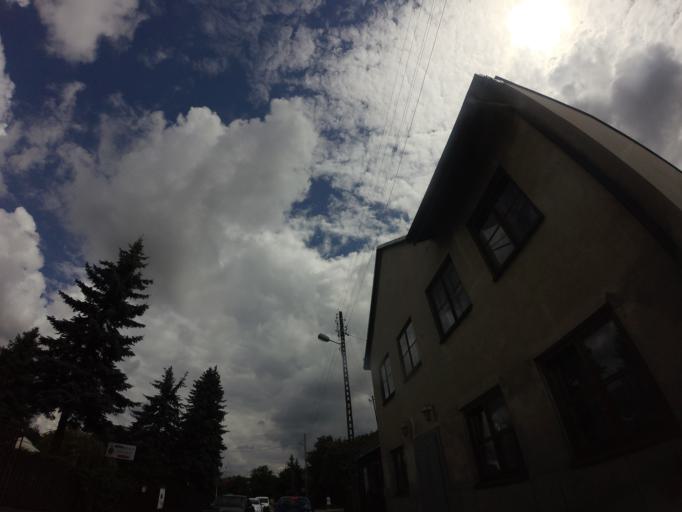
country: PL
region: Lublin Voivodeship
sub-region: Powiat pulawski
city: Kazimierz Dolny
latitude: 51.3235
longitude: 21.9477
